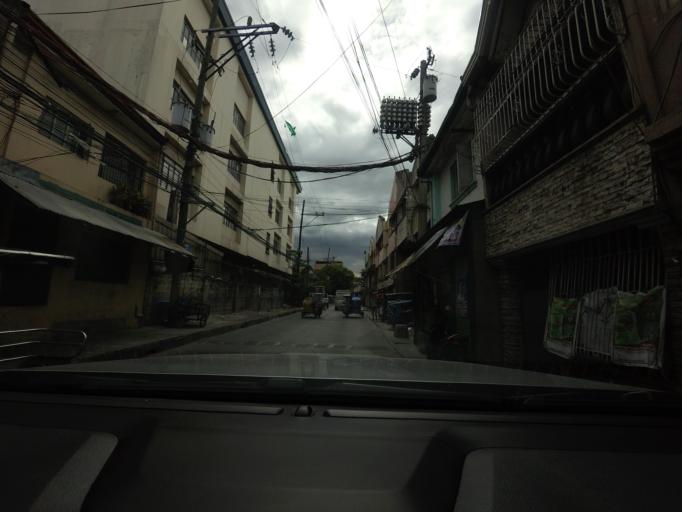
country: PH
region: Calabarzon
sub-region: Province of Rizal
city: Pateros
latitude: 14.5628
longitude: 121.0875
